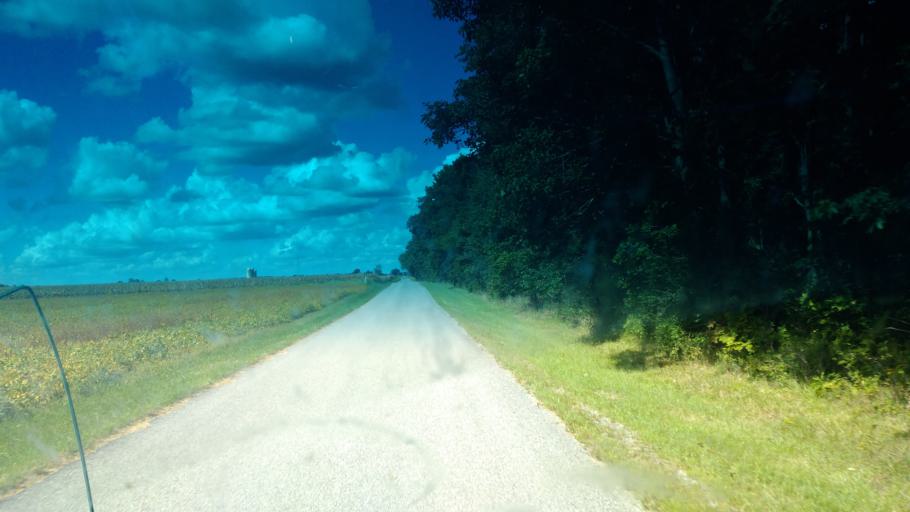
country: US
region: Ohio
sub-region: Hardin County
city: Kenton
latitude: 40.5081
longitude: -83.5390
